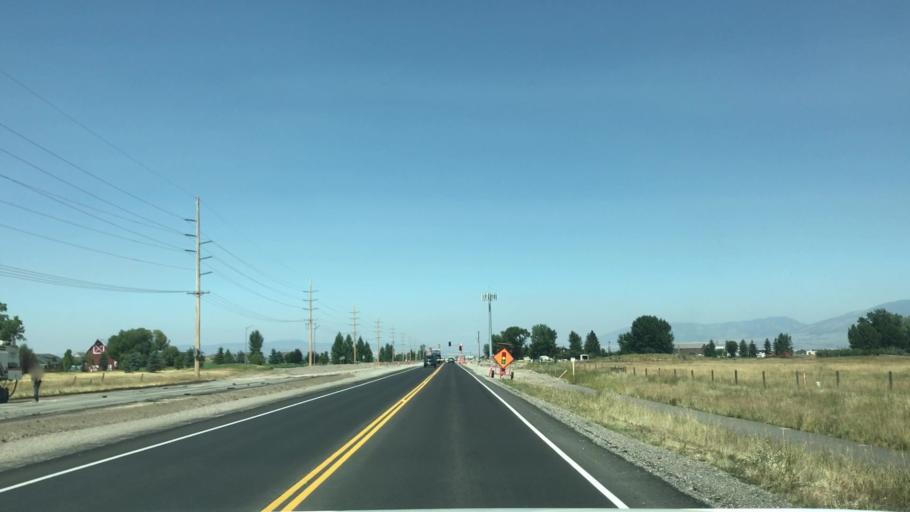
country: US
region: Montana
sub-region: Gallatin County
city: Belgrade
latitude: 45.7192
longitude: -111.1851
